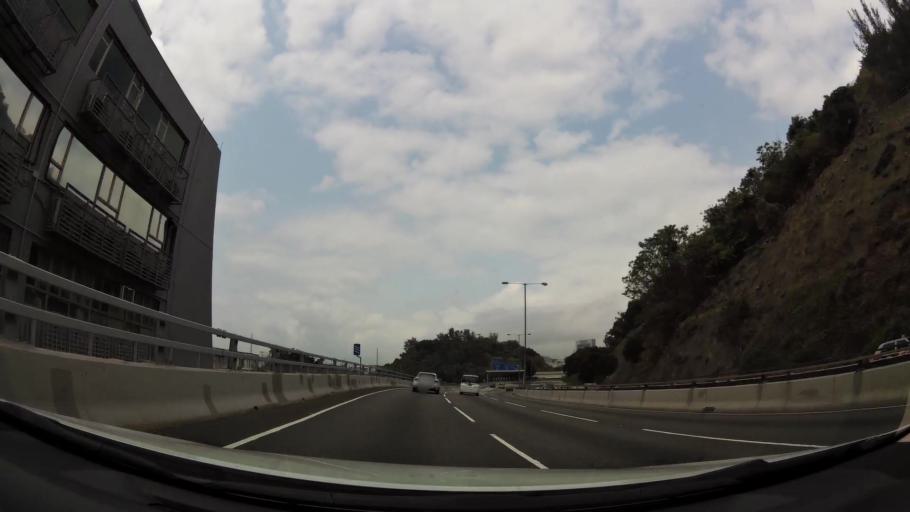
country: HK
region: Sham Shui Po
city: Sham Shui Po
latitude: 22.3399
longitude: 114.1472
